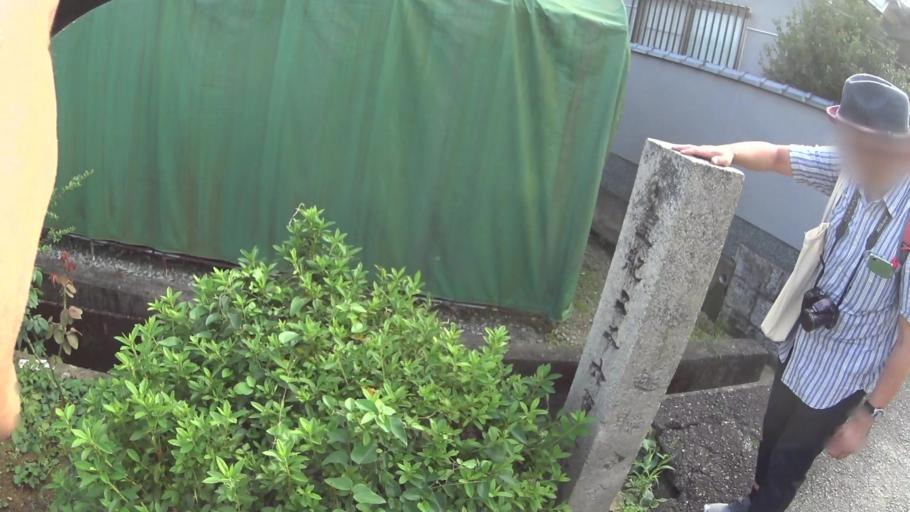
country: JP
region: Nara
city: Kashihara-shi
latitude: 34.4654
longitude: 135.7980
